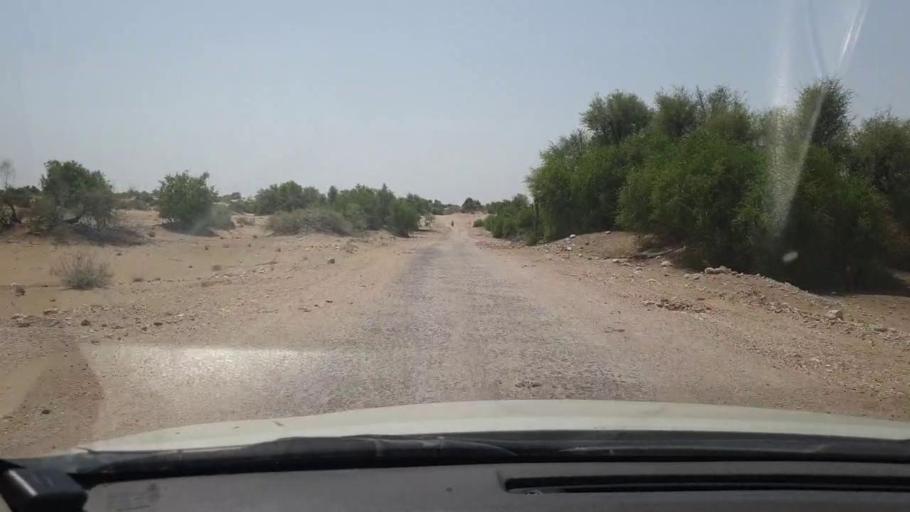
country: PK
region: Sindh
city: Rohri
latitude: 27.3175
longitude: 69.2794
